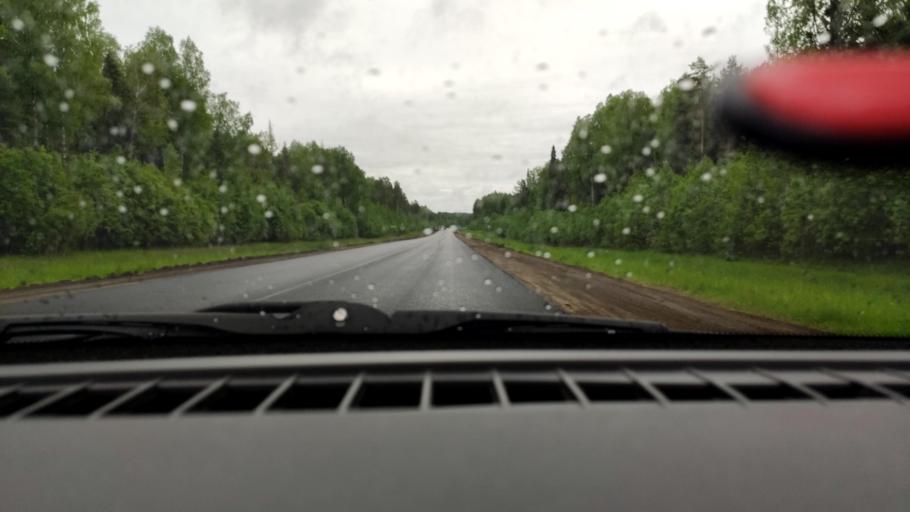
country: RU
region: Perm
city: Karagay
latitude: 58.2469
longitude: 54.9315
